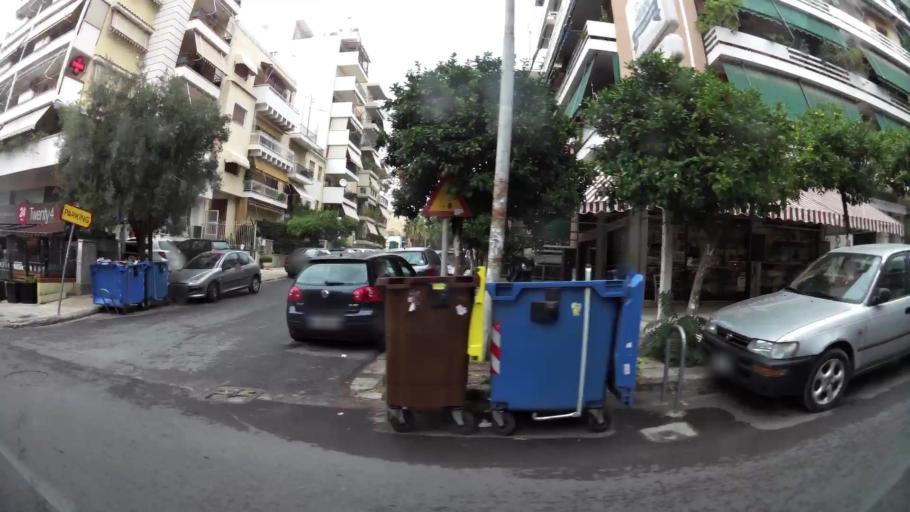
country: GR
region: Attica
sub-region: Nomarchia Athinas
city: Vyronas
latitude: 37.9640
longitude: 23.7577
